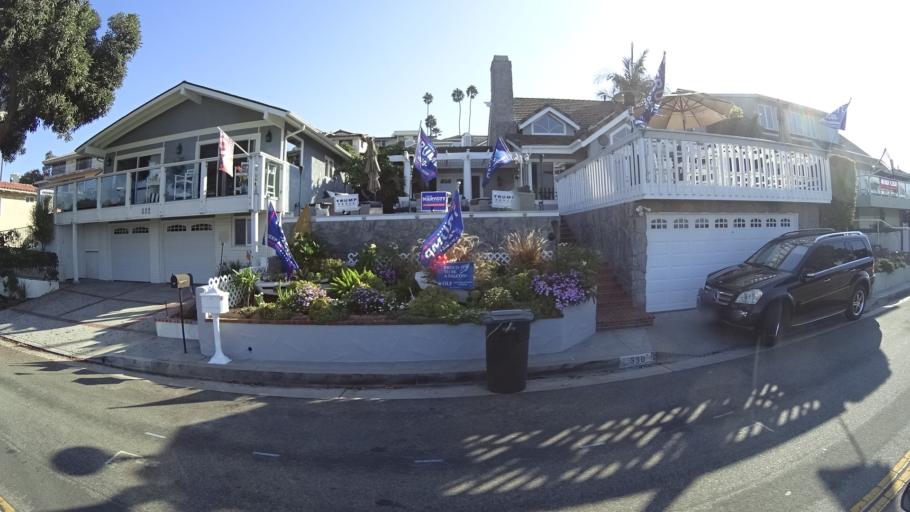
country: US
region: California
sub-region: Orange County
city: San Clemente
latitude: 33.4080
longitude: -117.5930
